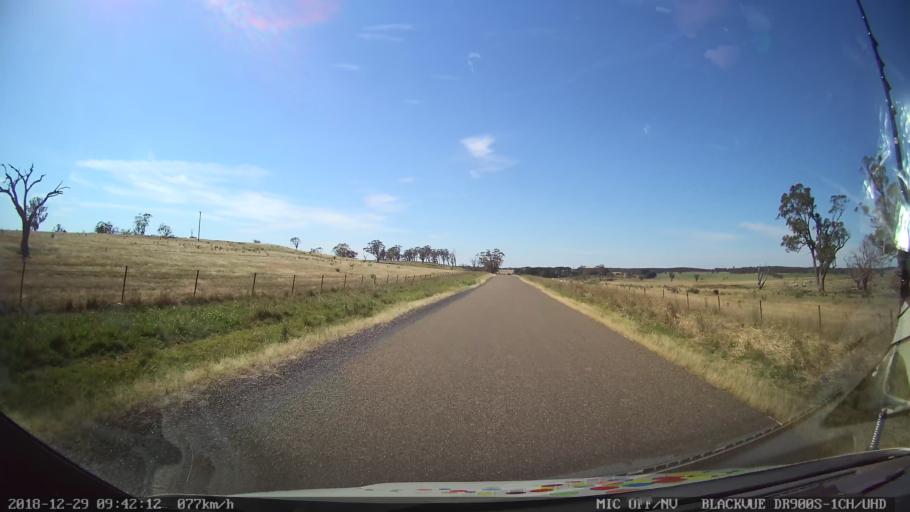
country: AU
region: New South Wales
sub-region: Upper Lachlan Shire
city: Crookwell
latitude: -34.6672
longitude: 149.4193
